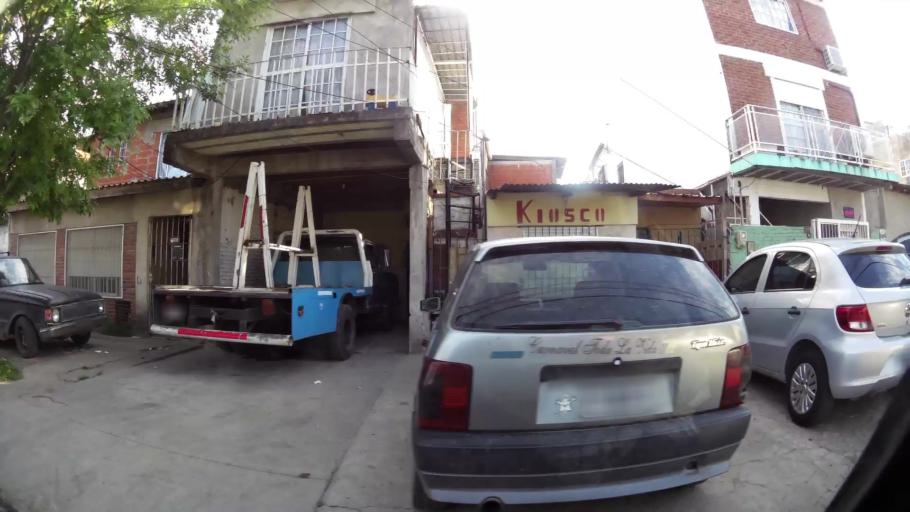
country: AR
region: Buenos Aires
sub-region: Partido de Lanus
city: Lanus
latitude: -34.7066
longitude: -58.3523
